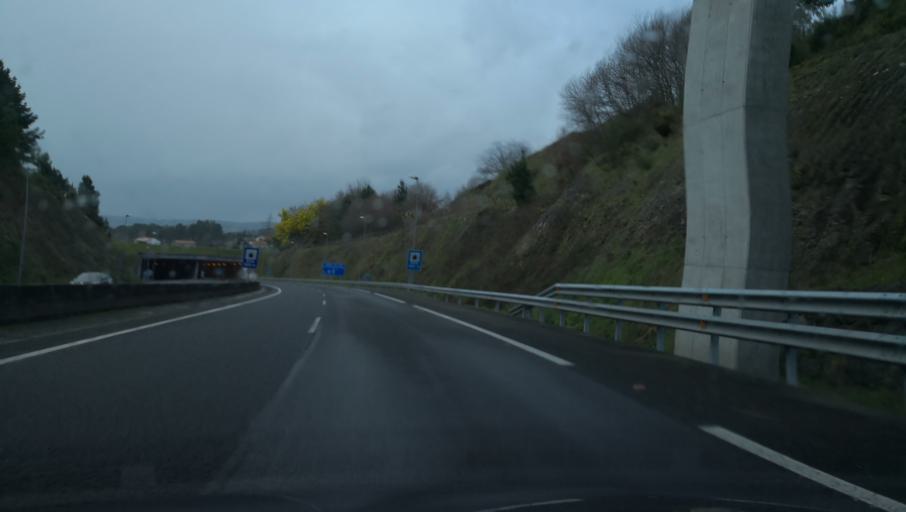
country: ES
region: Galicia
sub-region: Provincia da Coruna
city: Ribeira
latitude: 42.7506
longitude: -8.3908
